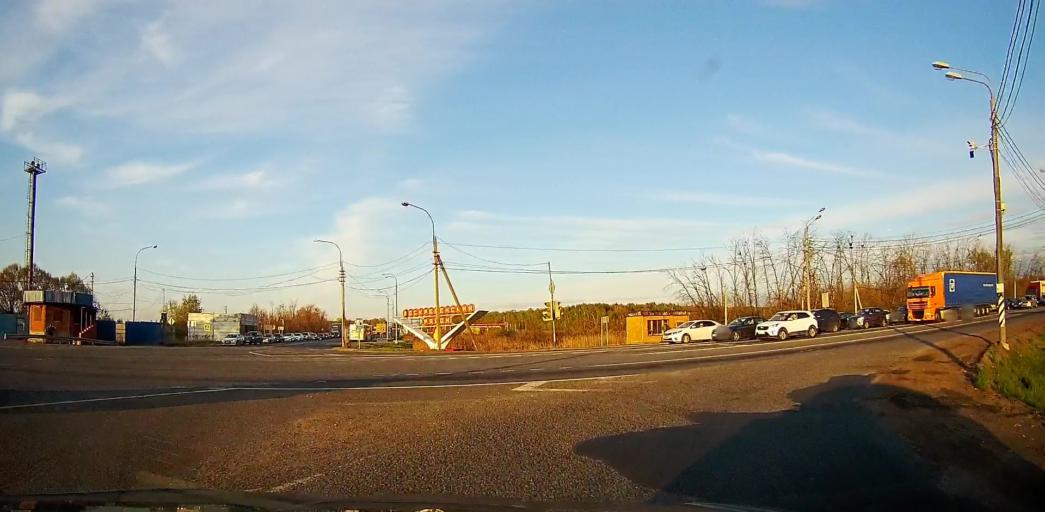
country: RU
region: Moskovskaya
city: Troitskoye
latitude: 55.2781
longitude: 38.4929
